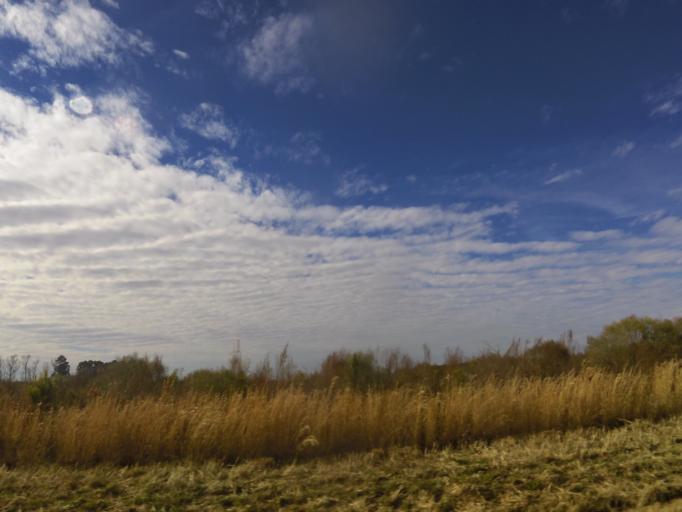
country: US
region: Virginia
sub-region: City of Franklin
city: Franklin
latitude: 36.6969
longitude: -76.8936
